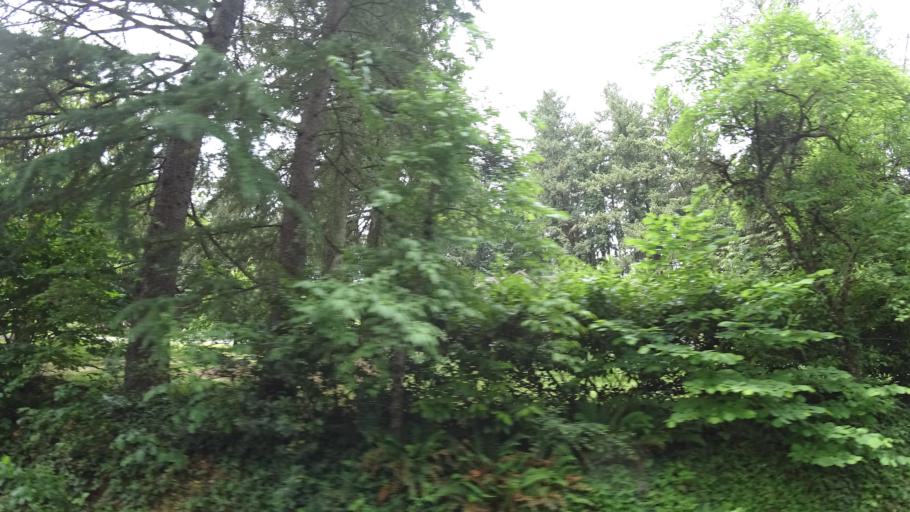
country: US
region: Oregon
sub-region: Washington County
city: Garden Home-Whitford
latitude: 45.4562
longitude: -122.7636
